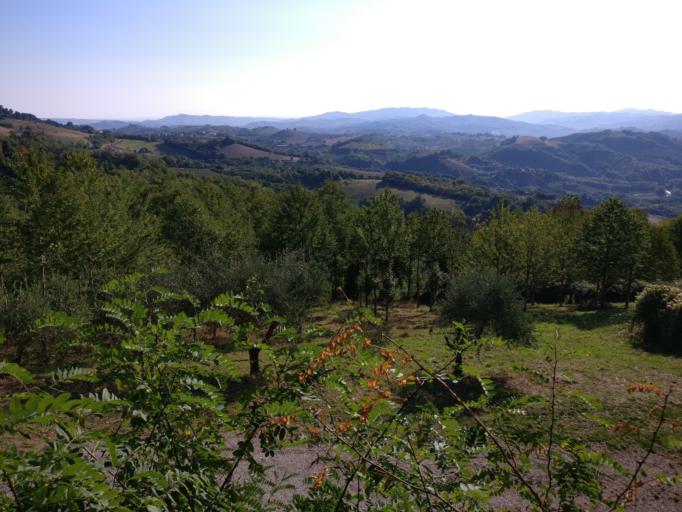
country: IT
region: The Marches
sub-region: Provincia di Ascoli Piceno
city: Montedinove
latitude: 42.9718
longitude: 13.5909
